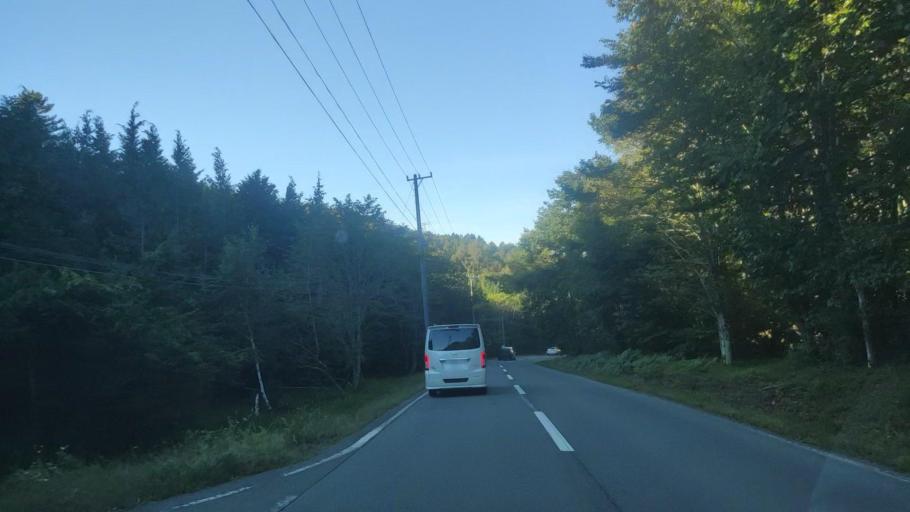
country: JP
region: Nagano
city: Kamimaruko
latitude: 36.2160
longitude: 138.2932
